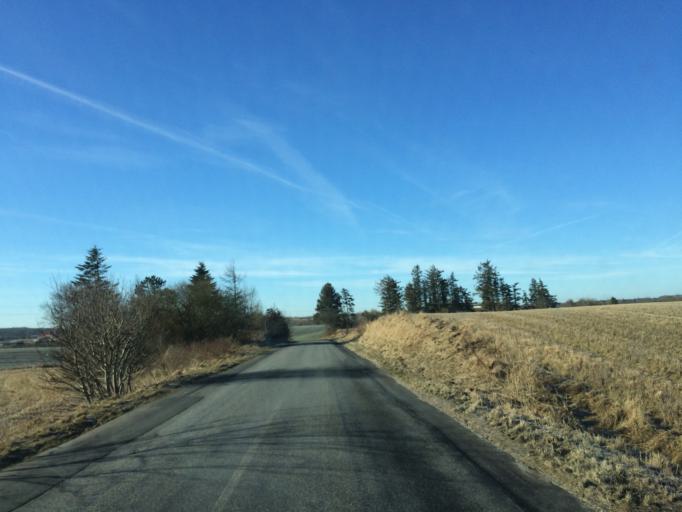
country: DK
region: North Denmark
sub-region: Mariagerfjord Kommune
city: Hobro
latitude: 56.6056
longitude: 9.6318
